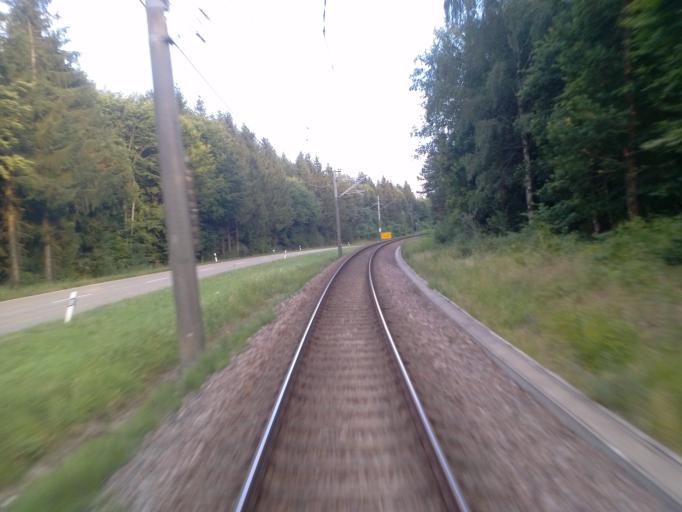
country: DE
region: Baden-Wuerttemberg
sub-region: Karlsruhe Region
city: Dobel
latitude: 48.8828
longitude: 8.5156
